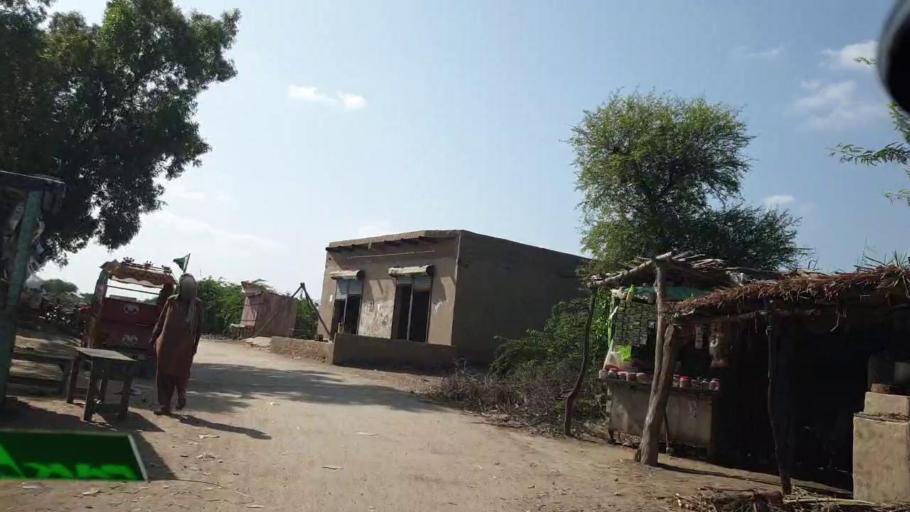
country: PK
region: Sindh
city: Tando Bago
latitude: 24.6756
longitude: 69.1950
